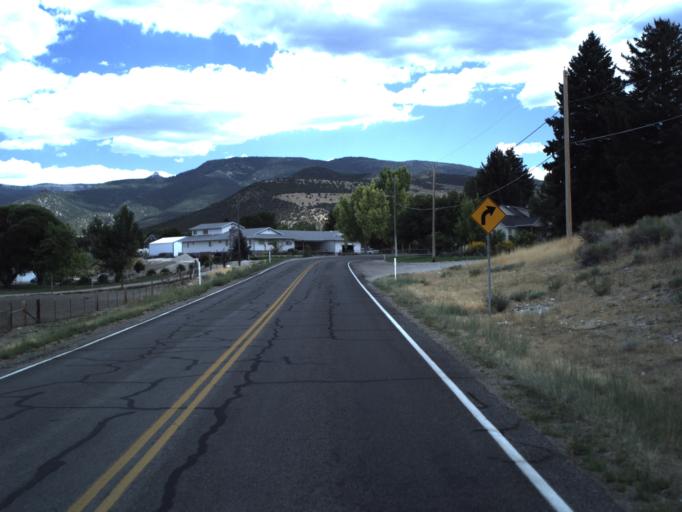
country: US
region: Utah
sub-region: Sanpete County
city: Centerfield
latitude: 39.1184
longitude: -111.7119
